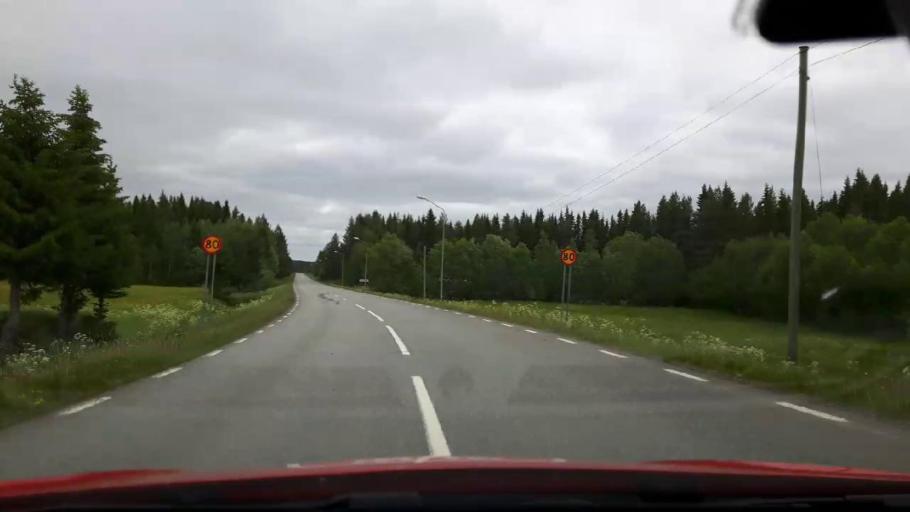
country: SE
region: Jaemtland
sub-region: Stroemsunds Kommun
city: Stroemsund
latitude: 63.5479
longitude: 15.4079
